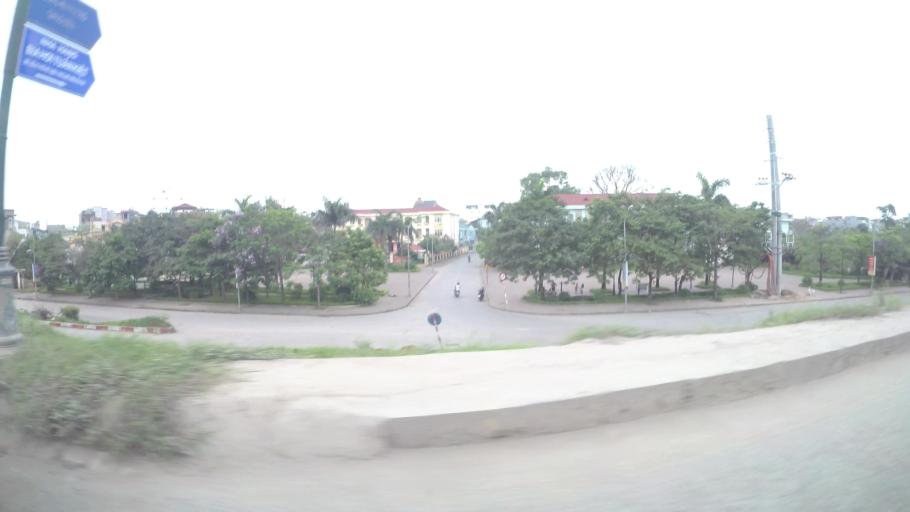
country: VN
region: Ha Noi
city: Trau Quy
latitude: 21.0634
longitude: 105.9193
